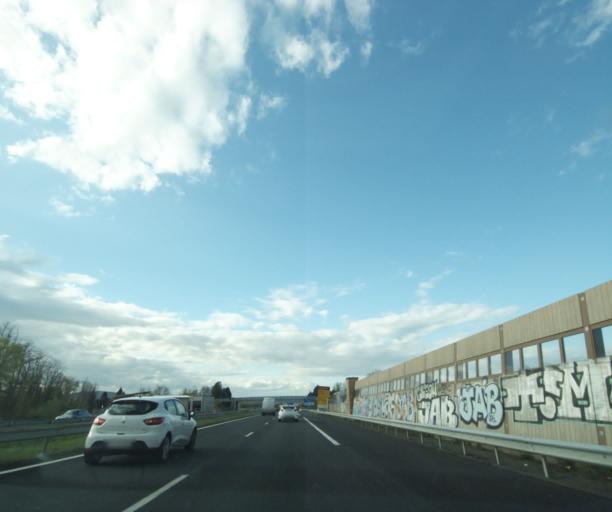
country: FR
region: Rhone-Alpes
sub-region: Departement du Rhone
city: Les Cheres
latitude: 45.8847
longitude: 4.7376
